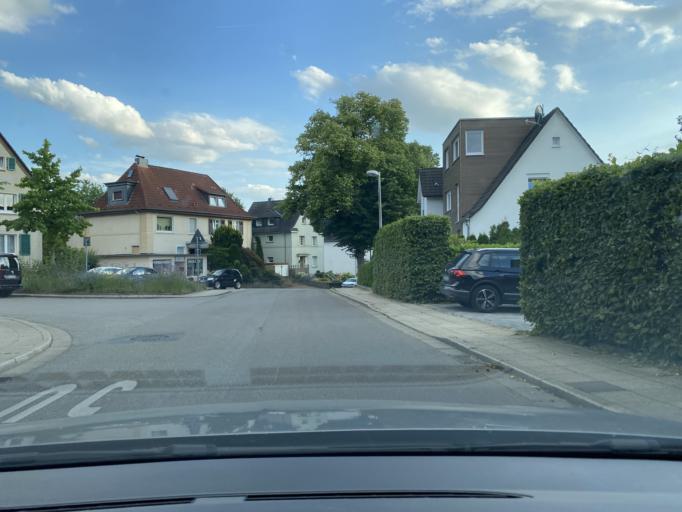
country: DE
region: North Rhine-Westphalia
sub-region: Regierungsbezirk Dusseldorf
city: Heiligenhaus
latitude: 51.3677
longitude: 6.9526
